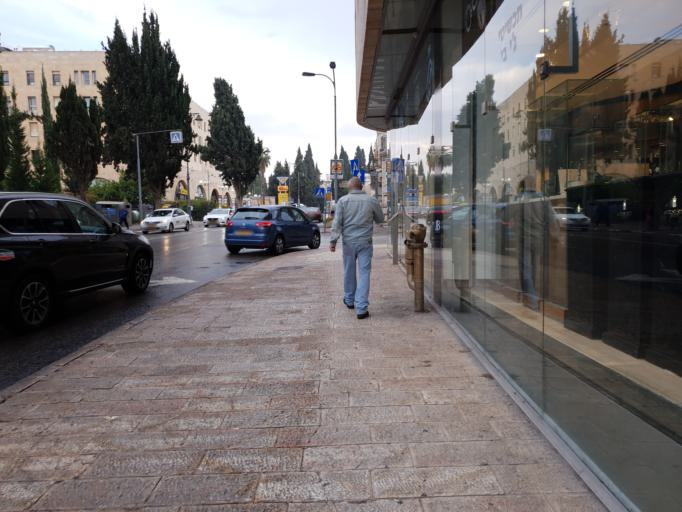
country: IL
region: Jerusalem
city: West Jerusalem
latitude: 31.7763
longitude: 35.2221
